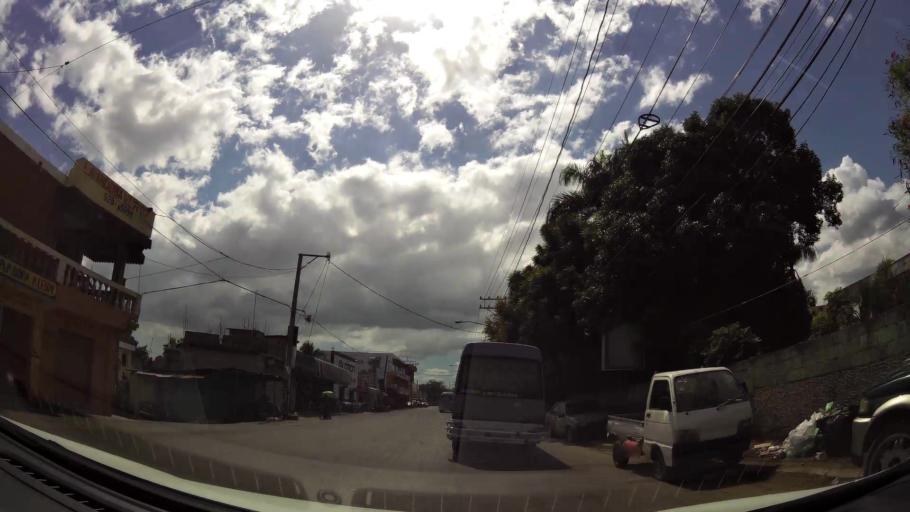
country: DO
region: San Cristobal
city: San Cristobal
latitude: 18.4208
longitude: -70.0999
